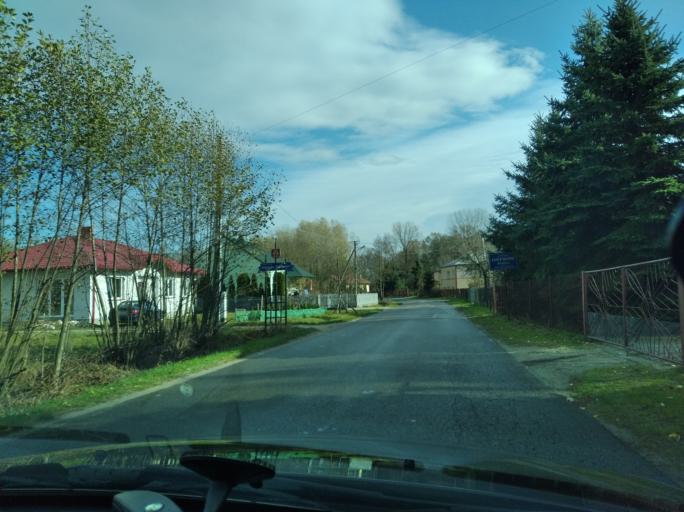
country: PL
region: Subcarpathian Voivodeship
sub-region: Powiat ropczycko-sedziszowski
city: Ostrow
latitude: 50.0956
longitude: 21.6432
